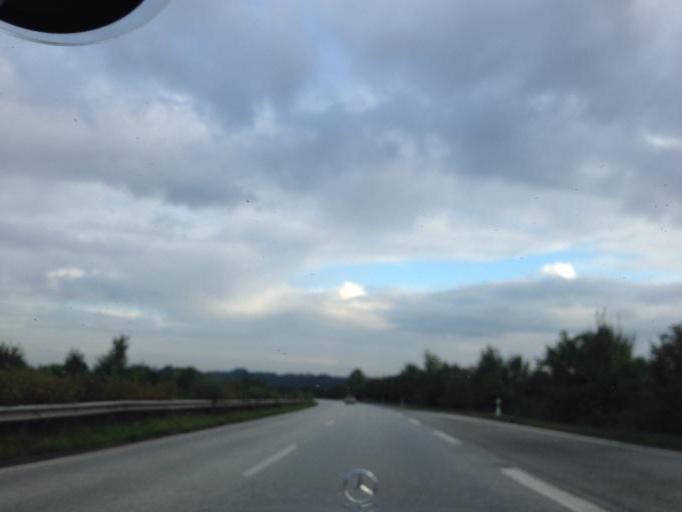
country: DE
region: Schleswig-Holstein
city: Rumpel
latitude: 53.7797
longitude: 10.3272
